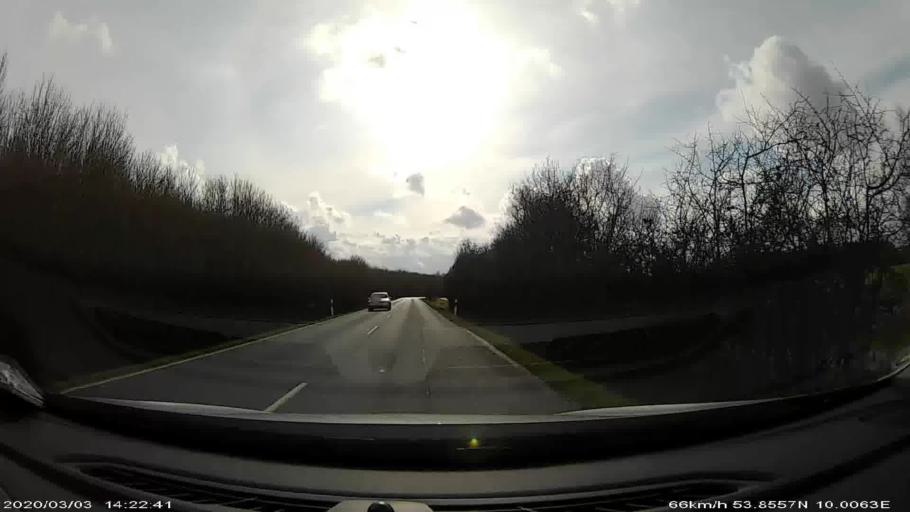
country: DE
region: Schleswig-Holstein
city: Kattendorf
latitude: 53.8556
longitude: 10.0062
